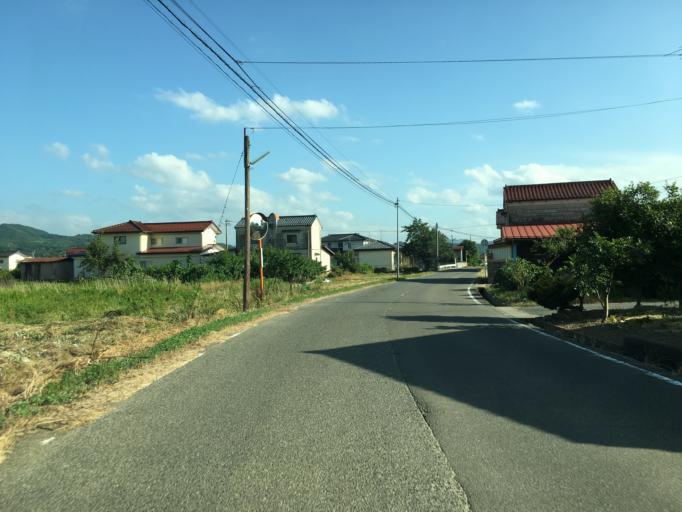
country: JP
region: Fukushima
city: Yanagawamachi-saiwaicho
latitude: 37.8361
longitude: 140.5845
